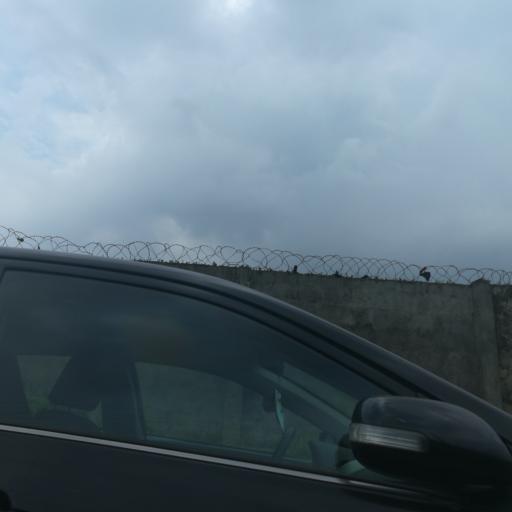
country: NG
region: Lagos
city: Ojota
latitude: 6.5812
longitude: 3.3833
